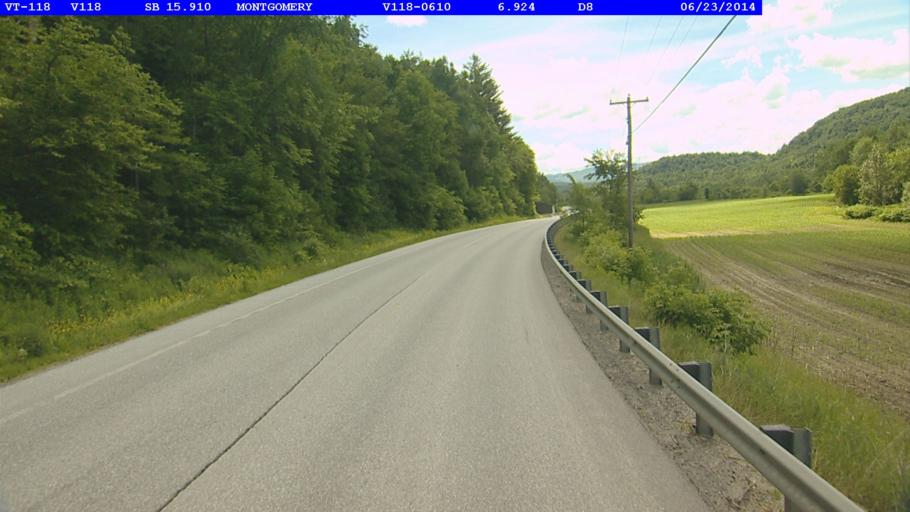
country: US
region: Vermont
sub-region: Franklin County
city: Richford
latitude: 44.8928
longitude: -72.6221
